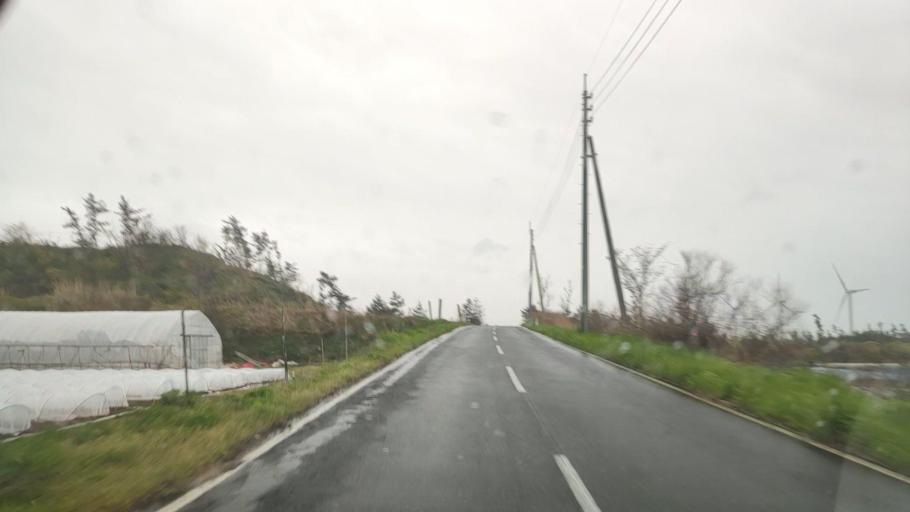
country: JP
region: Akita
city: Noshiromachi
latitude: 40.0892
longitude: 139.9604
